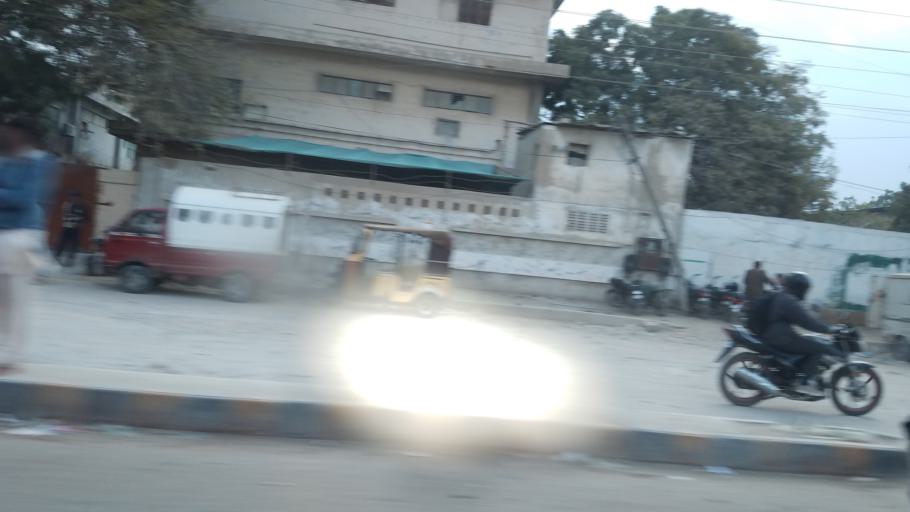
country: PK
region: Sindh
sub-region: Karachi District
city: Karachi
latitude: 24.9410
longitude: 67.0851
